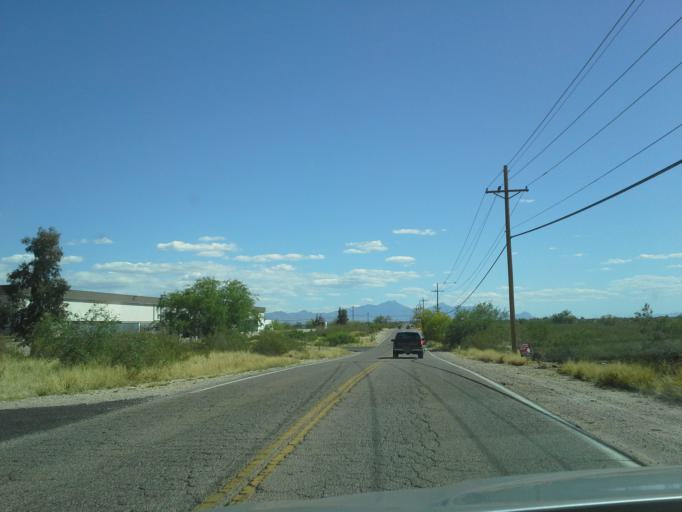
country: US
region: Arizona
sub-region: Pima County
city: Tucson
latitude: 32.1336
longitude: -110.8580
